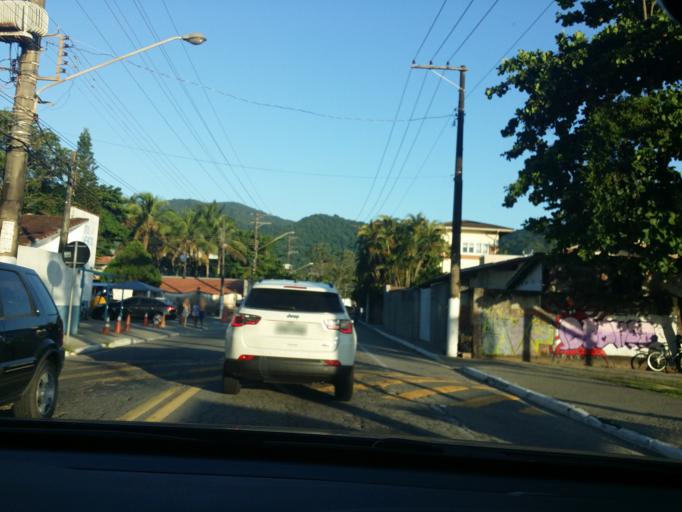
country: BR
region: Sao Paulo
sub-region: Sao Sebastiao
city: Sao Sebastiao
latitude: -23.7836
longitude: -45.6298
